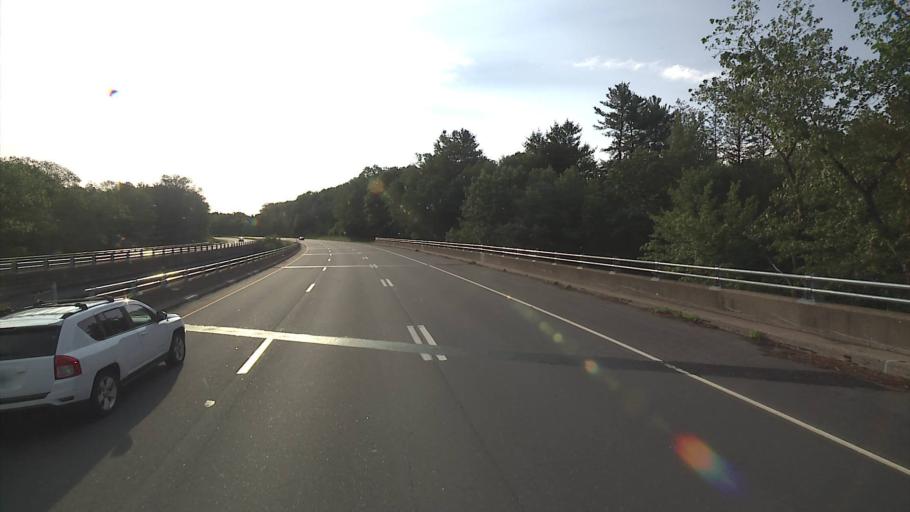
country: US
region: Connecticut
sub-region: New London County
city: Montville Center
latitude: 41.5606
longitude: -72.1590
